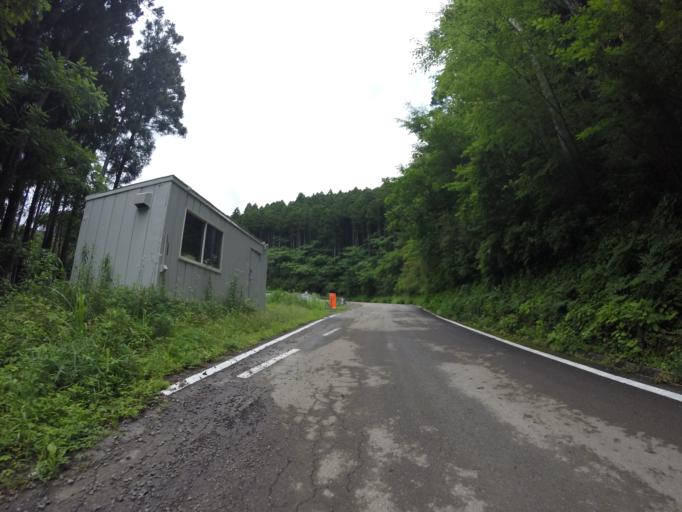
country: JP
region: Shizuoka
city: Shizuoka-shi
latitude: 35.0473
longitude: 138.3112
